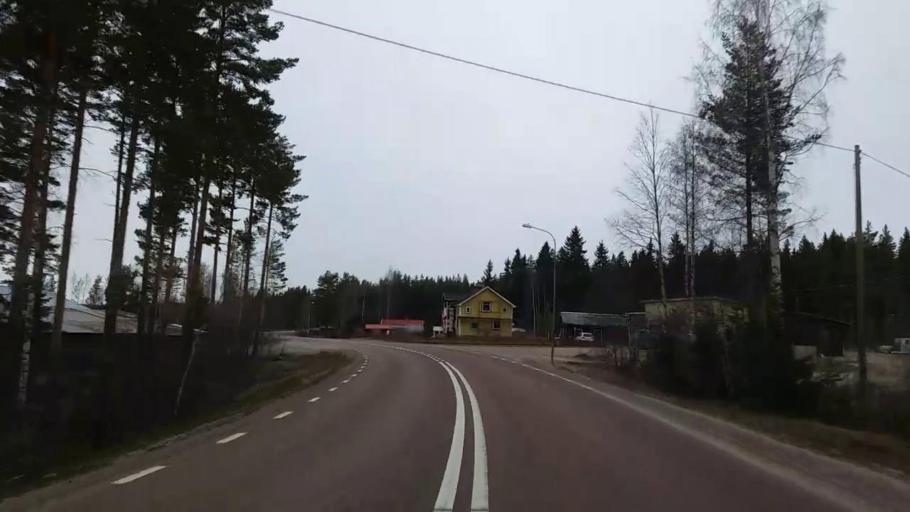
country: SE
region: Gaevleborg
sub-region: Ovanakers Kommun
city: Edsbyn
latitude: 61.2522
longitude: 15.8916
